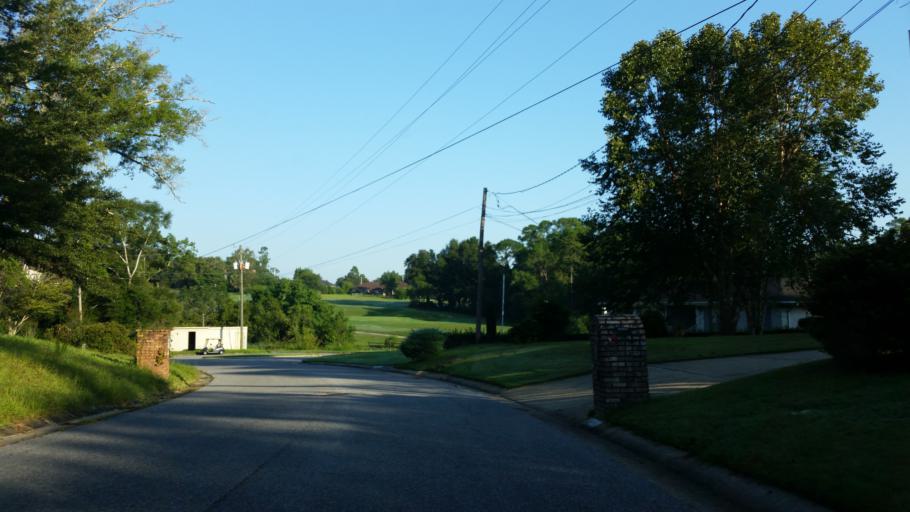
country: US
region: Florida
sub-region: Escambia County
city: Ferry Pass
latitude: 30.5416
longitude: -87.2295
